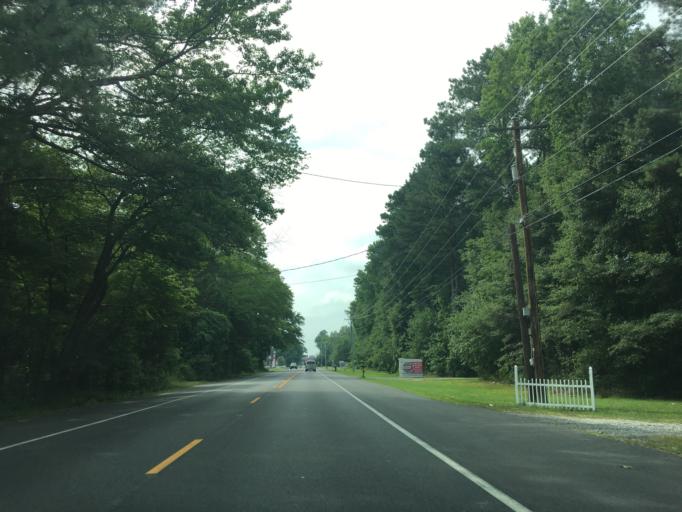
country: US
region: Delaware
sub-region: Sussex County
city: Millsboro
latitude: 38.5620
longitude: -75.2689
